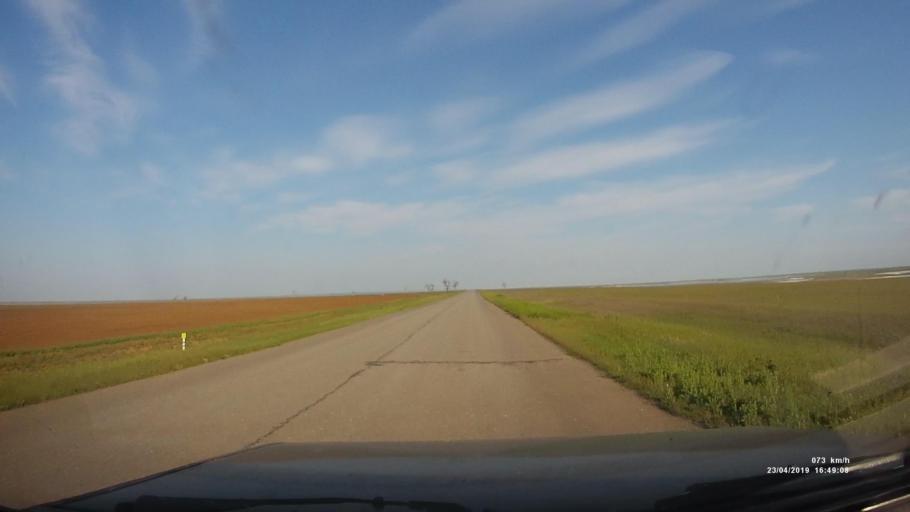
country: RU
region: Kalmykiya
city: Priyutnoye
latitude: 46.3321
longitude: 43.2720
